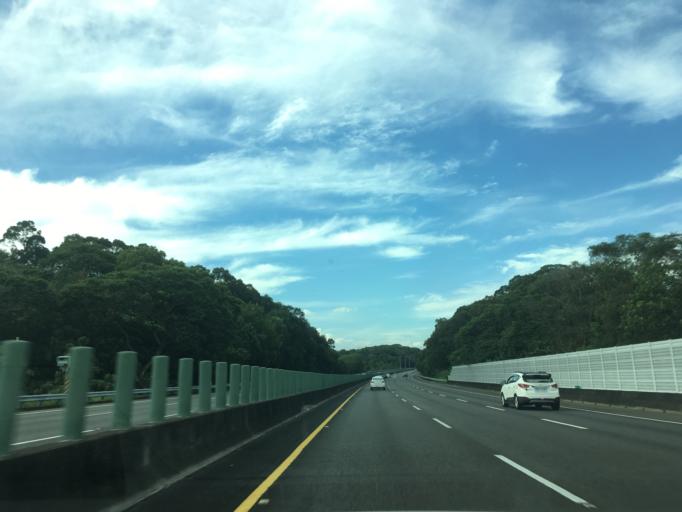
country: TW
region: Taiwan
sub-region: Chiayi
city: Jiayi Shi
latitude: 23.5697
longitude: 120.5055
